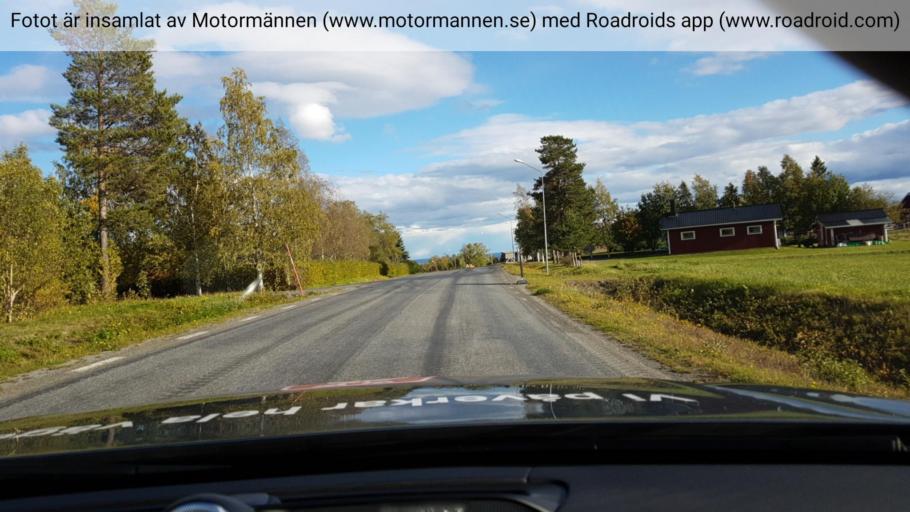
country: SE
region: Jaemtland
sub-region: Krokoms Kommun
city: Krokom
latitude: 63.1834
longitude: 14.0575
